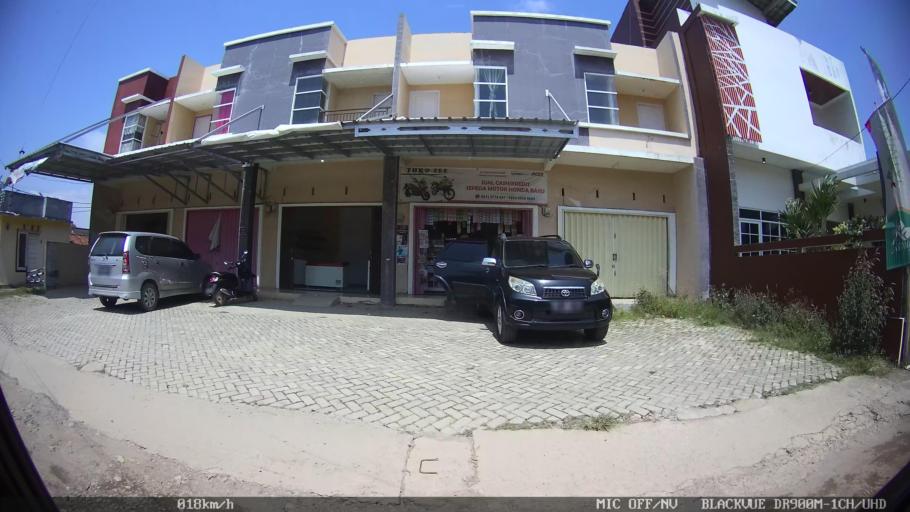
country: ID
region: Lampung
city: Kedaton
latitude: -5.3556
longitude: 105.2765
